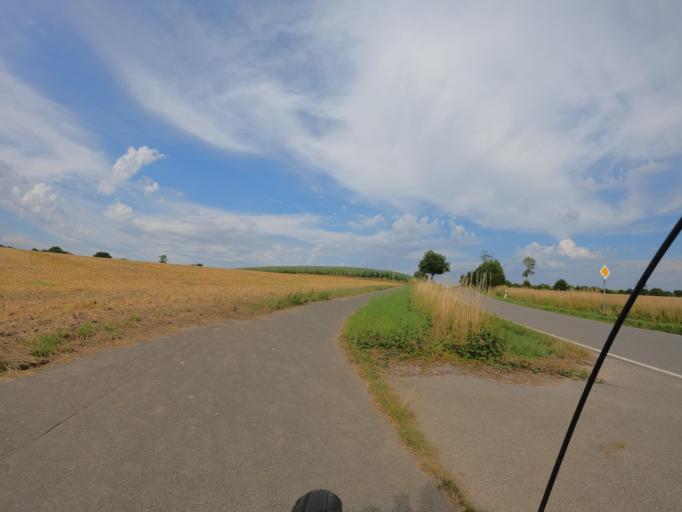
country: DE
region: Schleswig-Holstein
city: Steinberg
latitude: 54.7812
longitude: 9.7909
